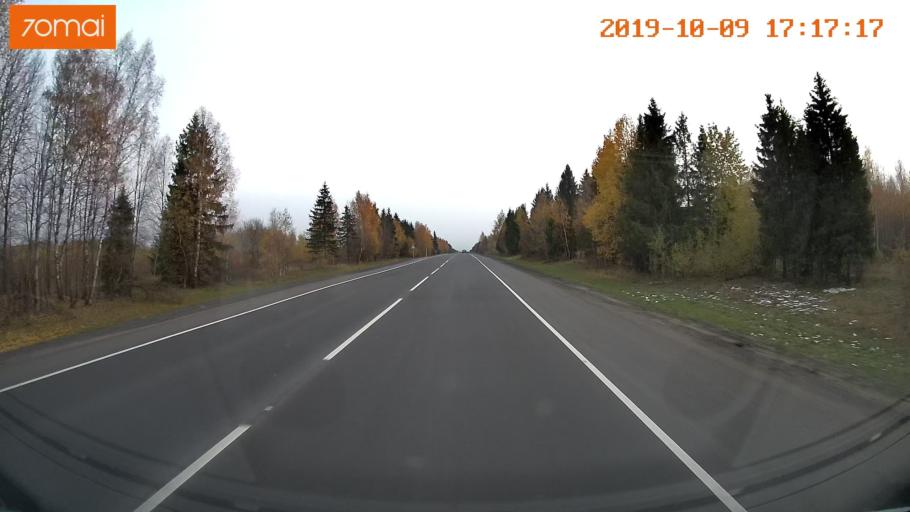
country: RU
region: Ivanovo
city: Furmanov
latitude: 57.2777
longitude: 41.1587
